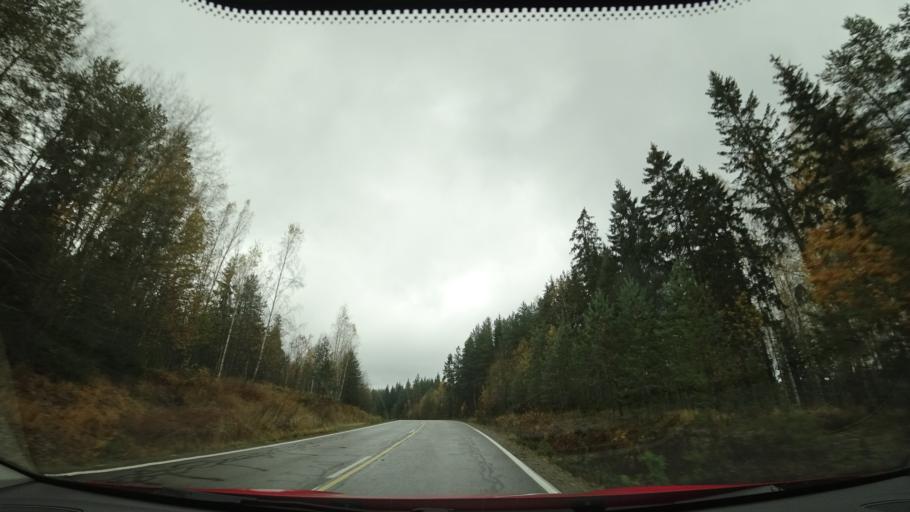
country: FI
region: Uusimaa
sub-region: Helsinki
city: Sibbo
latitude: 60.2745
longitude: 25.2020
